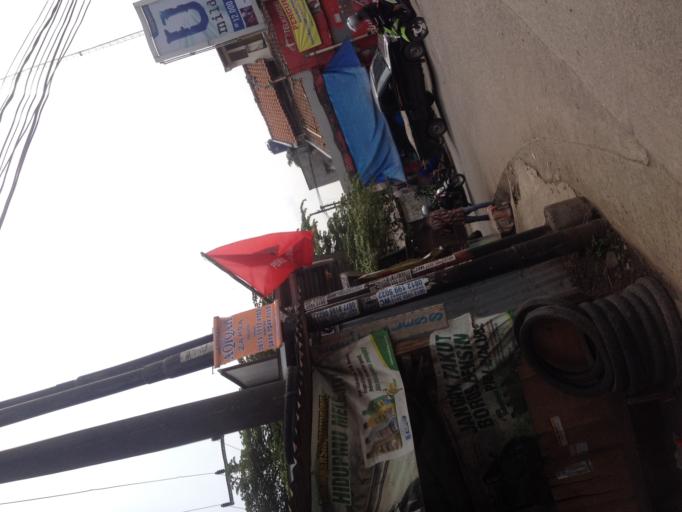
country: ID
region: West Java
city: Citeureup
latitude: -6.4551
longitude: 106.8963
